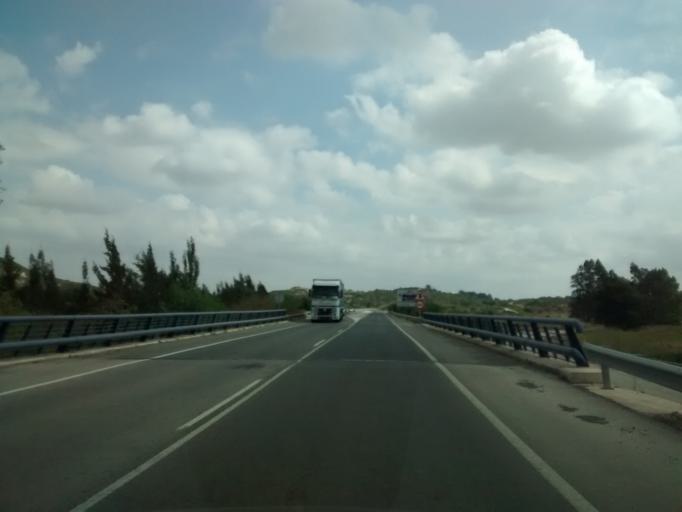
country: ES
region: Andalusia
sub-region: Provincia de Cadiz
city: Medina Sidonia
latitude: 36.4335
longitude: -6.0346
